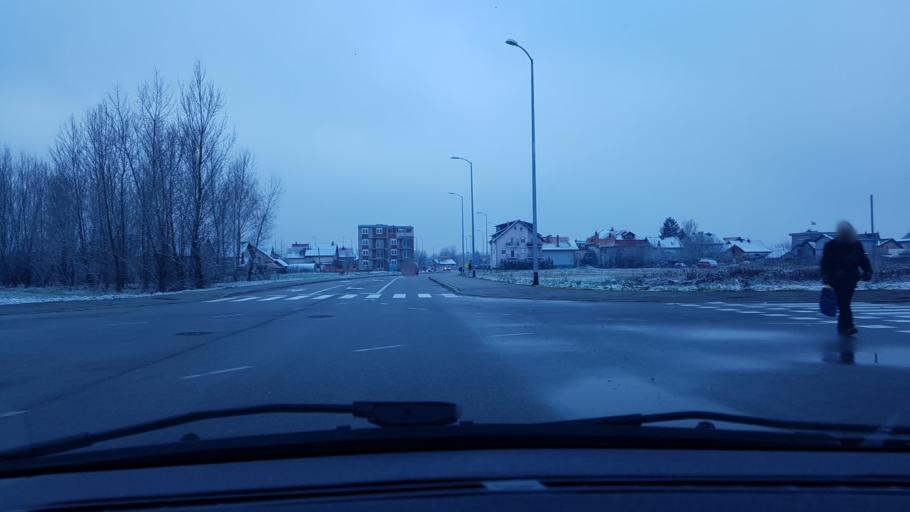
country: HR
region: Zagrebacka
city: Zapresic
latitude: 45.8575
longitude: 15.7976
